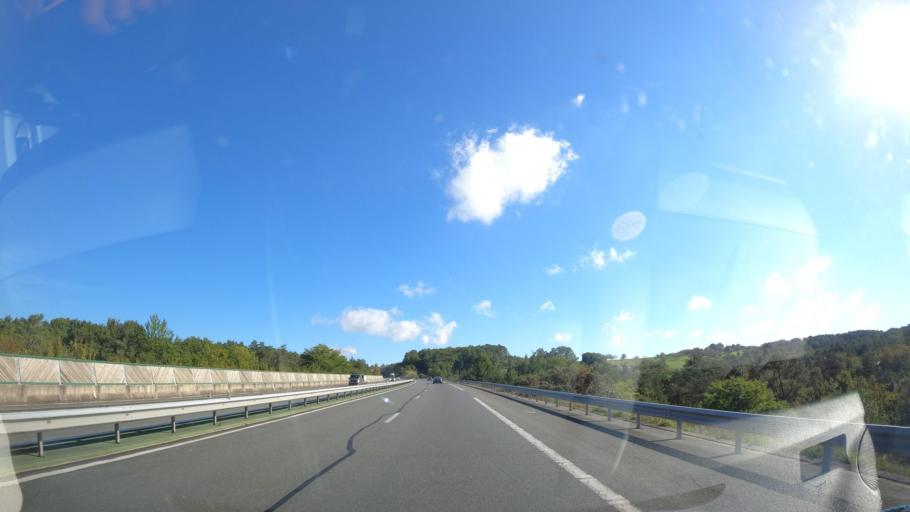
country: FR
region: Aquitaine
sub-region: Departement de la Dordogne
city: Bassillac
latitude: 45.1553
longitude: 0.8253
